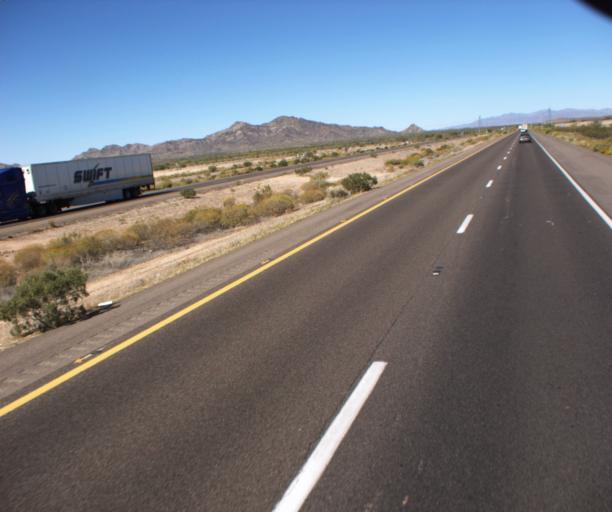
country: US
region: Arizona
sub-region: Maricopa County
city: Buckeye
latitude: 33.2147
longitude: -112.6448
